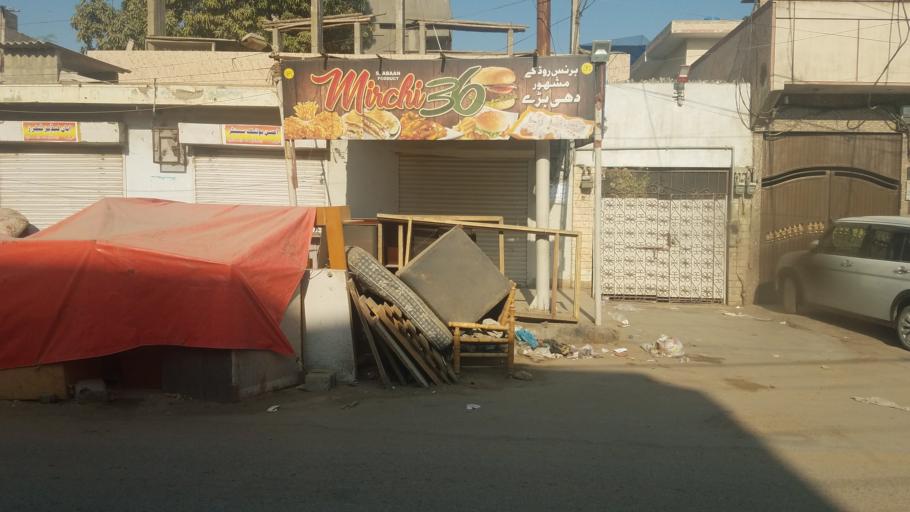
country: PK
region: Sindh
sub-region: Karachi District
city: Karachi
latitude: 24.9412
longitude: 67.0699
